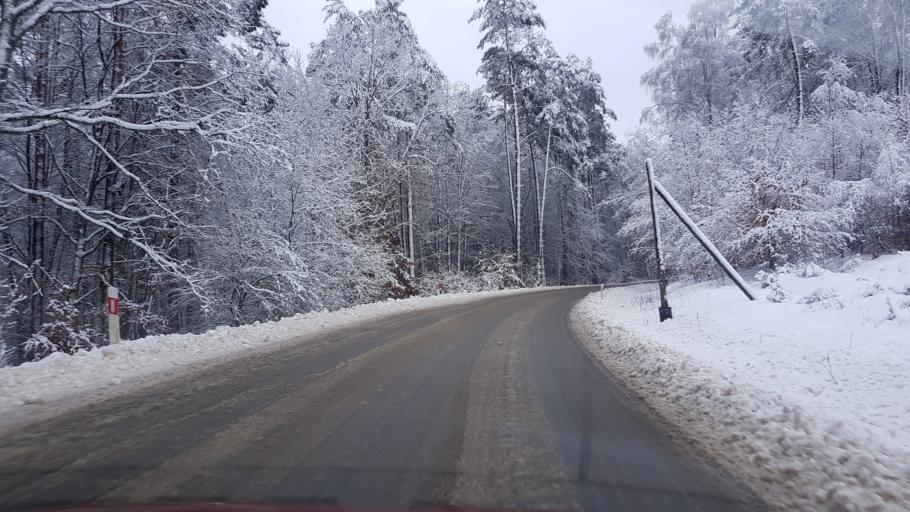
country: PL
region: West Pomeranian Voivodeship
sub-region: Powiat drawski
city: Zlocieniec
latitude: 53.5772
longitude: 16.0096
